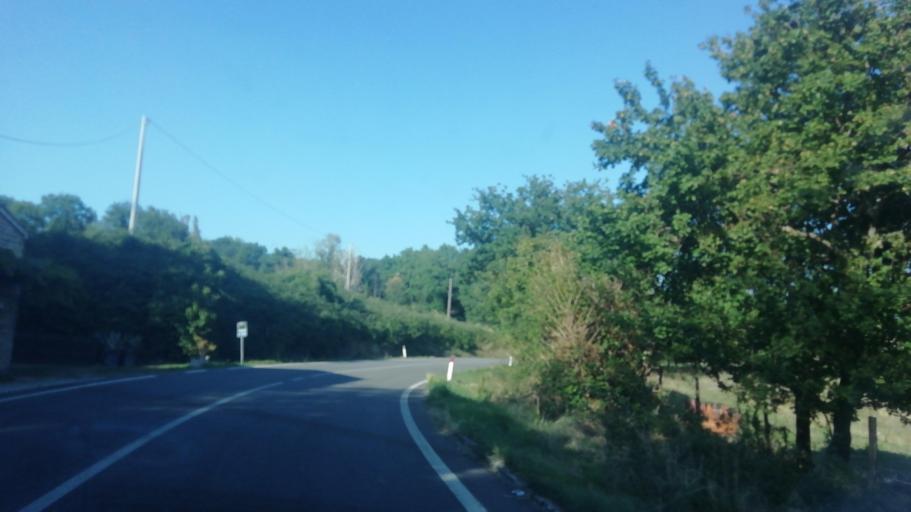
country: IT
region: The Marches
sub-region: Provincia di Pesaro e Urbino
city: Frontone
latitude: 43.5408
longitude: 12.7552
